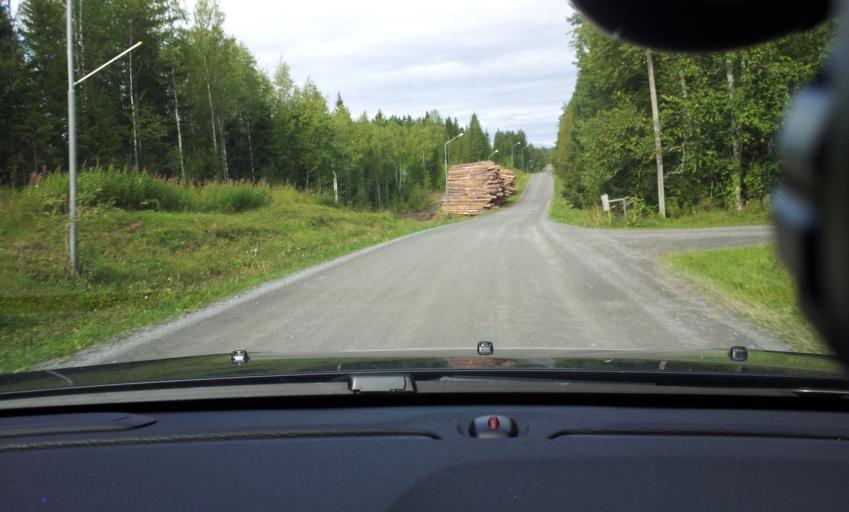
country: SE
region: Jaemtland
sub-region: Krokoms Kommun
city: Valla
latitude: 63.2594
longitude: 13.9269
